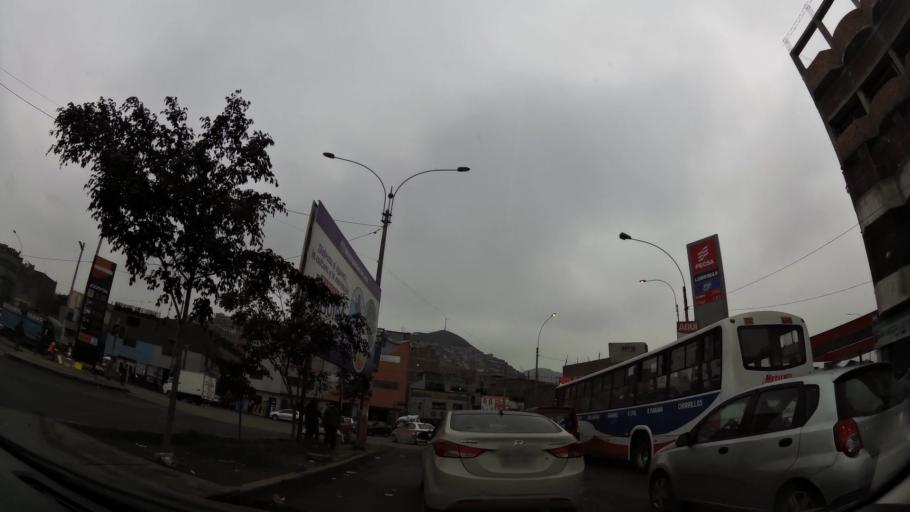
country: PE
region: Lima
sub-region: Lima
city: San Luis
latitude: -12.0631
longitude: -77.0027
